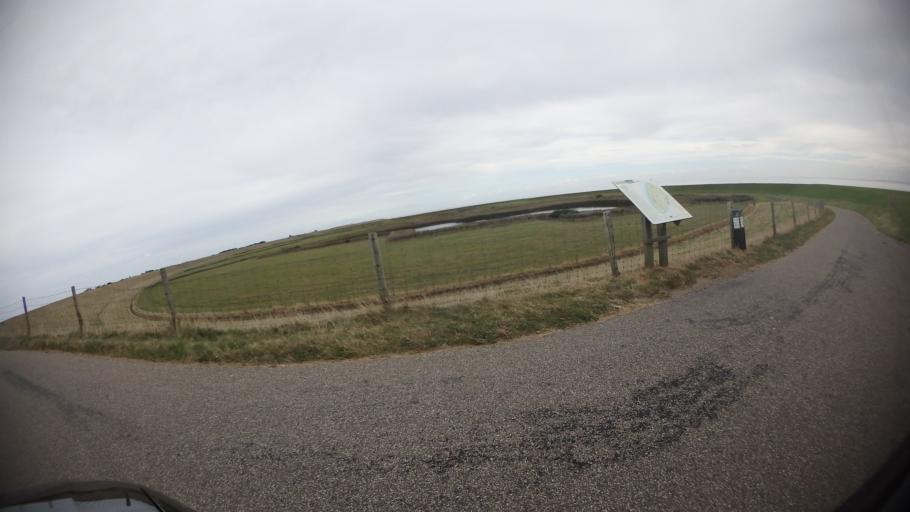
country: NL
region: North Holland
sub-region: Gemeente Texel
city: Den Burg
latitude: 53.0659
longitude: 4.8728
